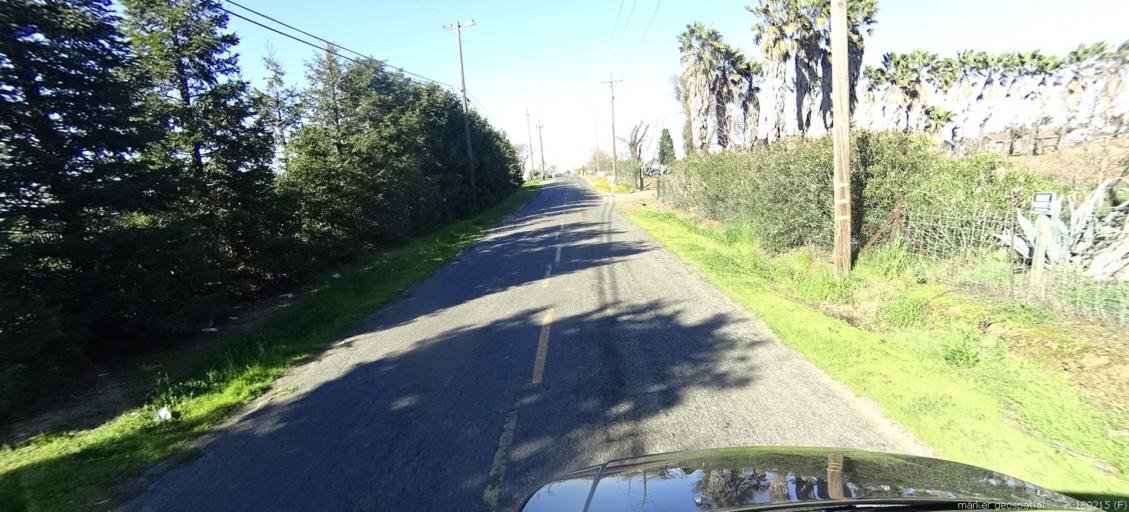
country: US
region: California
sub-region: Sacramento County
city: Rio Linda
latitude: 38.6877
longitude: -121.4754
